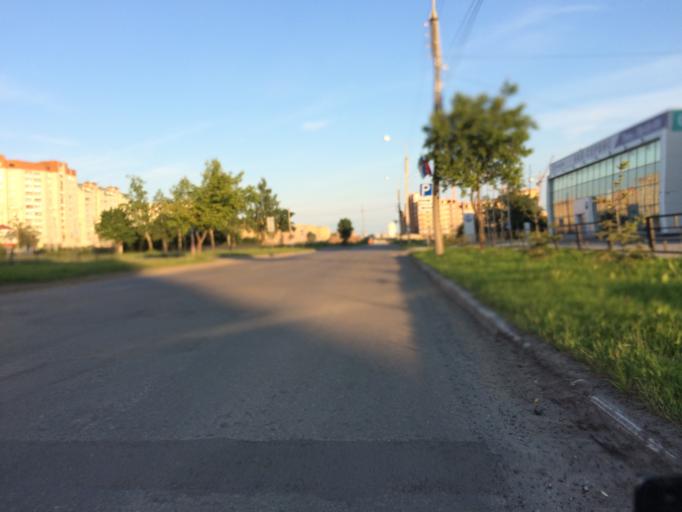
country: RU
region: Mariy-El
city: Medvedevo
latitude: 56.6412
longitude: 47.8335
